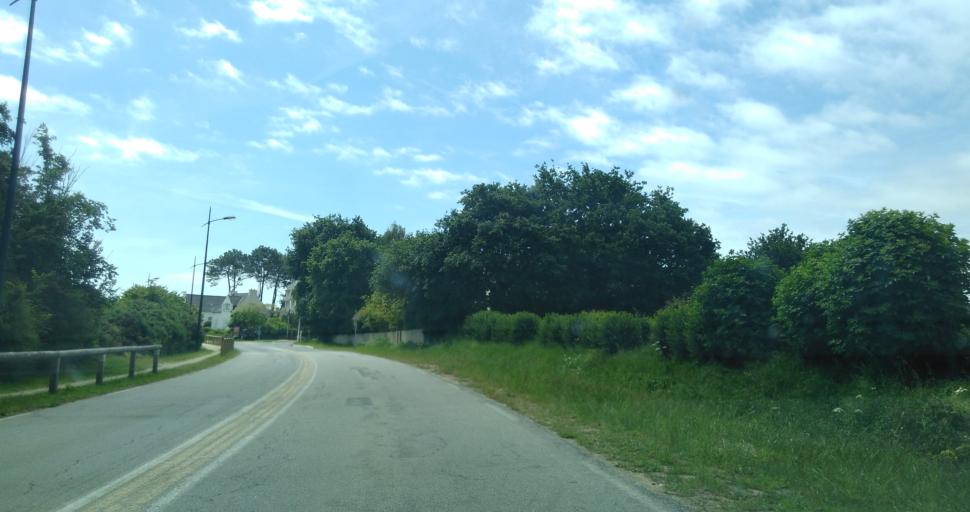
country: FR
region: Brittany
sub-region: Departement du Morbihan
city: La Trinite-sur-Mer
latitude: 47.5907
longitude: -3.0350
